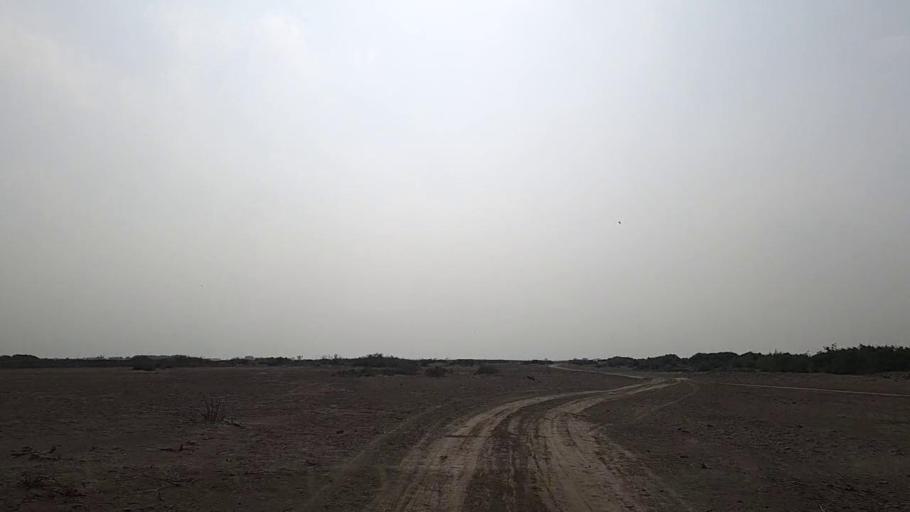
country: PK
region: Sindh
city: Gharo
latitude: 24.6715
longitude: 67.6419
